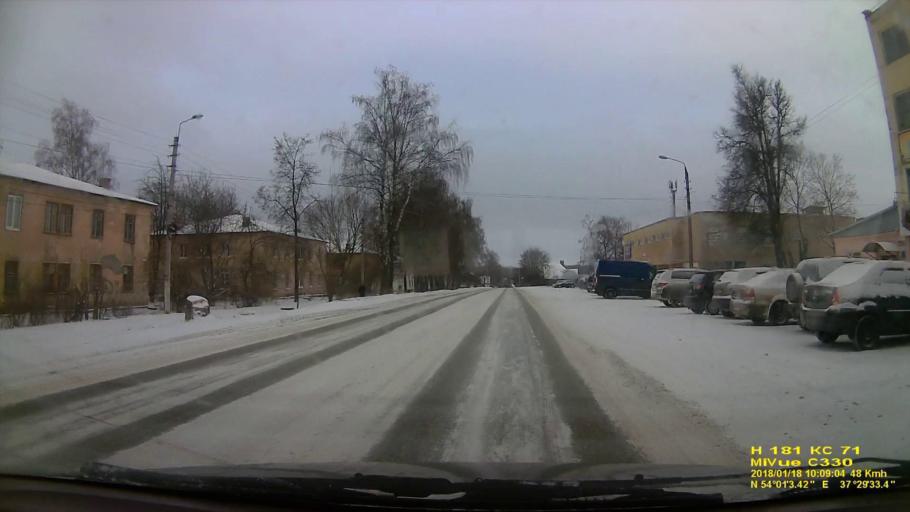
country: RU
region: Tula
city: Pervomayskiy
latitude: 54.0175
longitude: 37.4927
